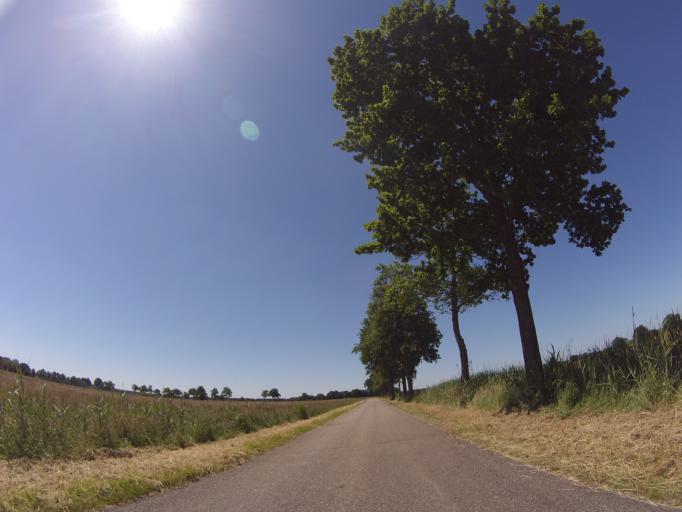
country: NL
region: Drenthe
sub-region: Gemeente Assen
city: Assen
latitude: 52.9498
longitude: 6.5700
